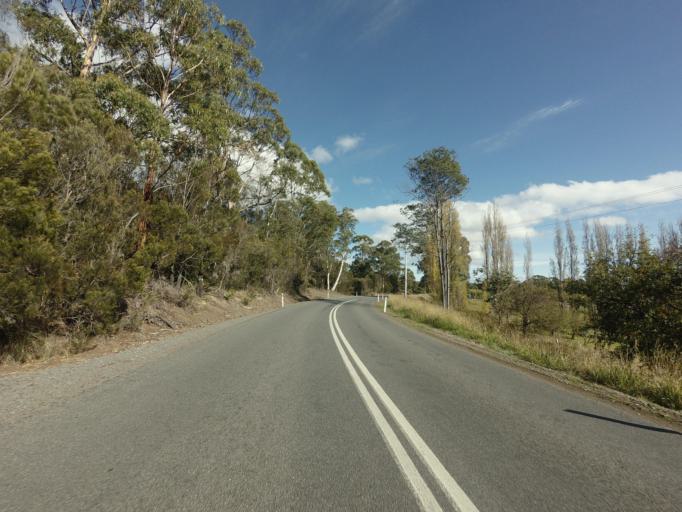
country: AU
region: Tasmania
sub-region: Clarence
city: Sandford
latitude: -43.0615
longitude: 147.8280
